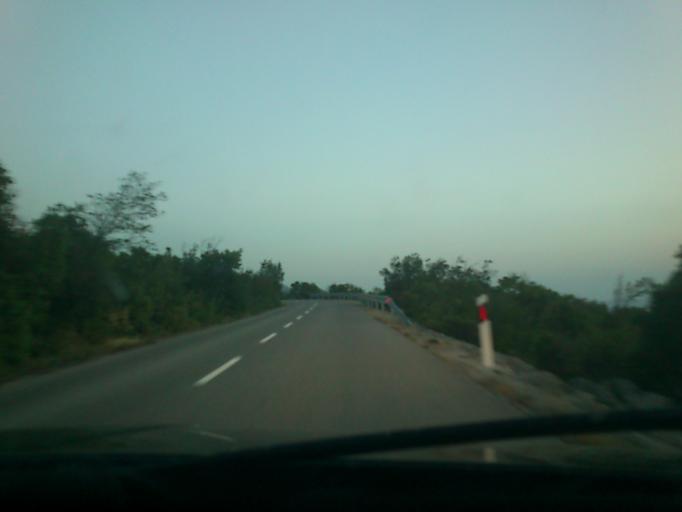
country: HR
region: Licko-Senjska
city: Senj
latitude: 44.9177
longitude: 14.9299
